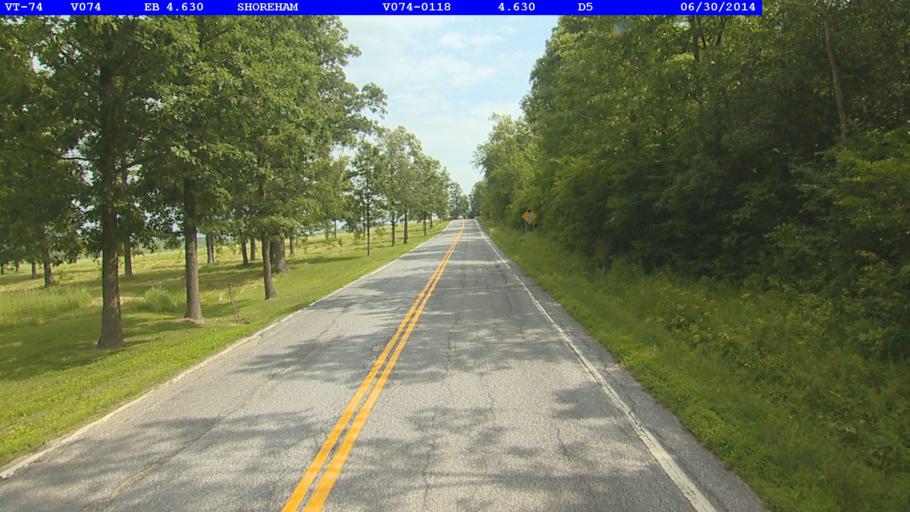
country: US
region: New York
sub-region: Essex County
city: Ticonderoga
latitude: 43.8913
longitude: -73.3194
